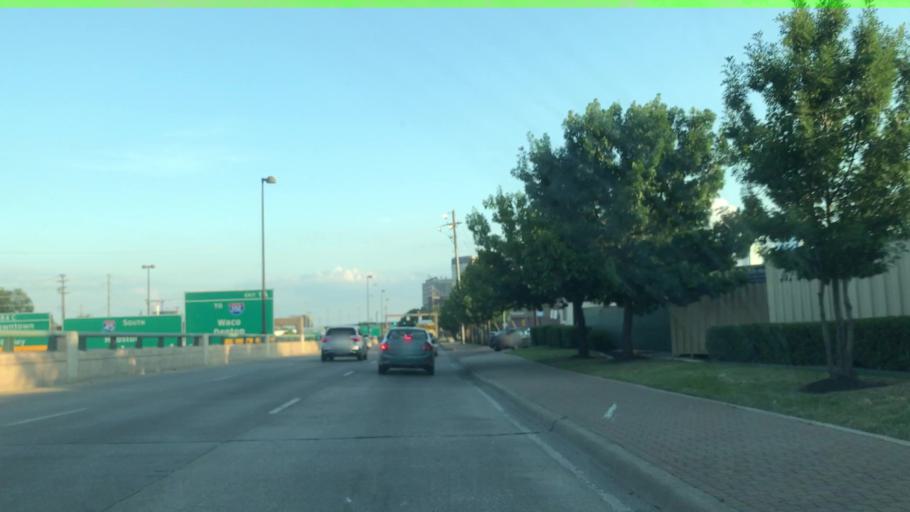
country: US
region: Texas
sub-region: Dallas County
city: Dallas
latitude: 32.8021
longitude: -96.7935
